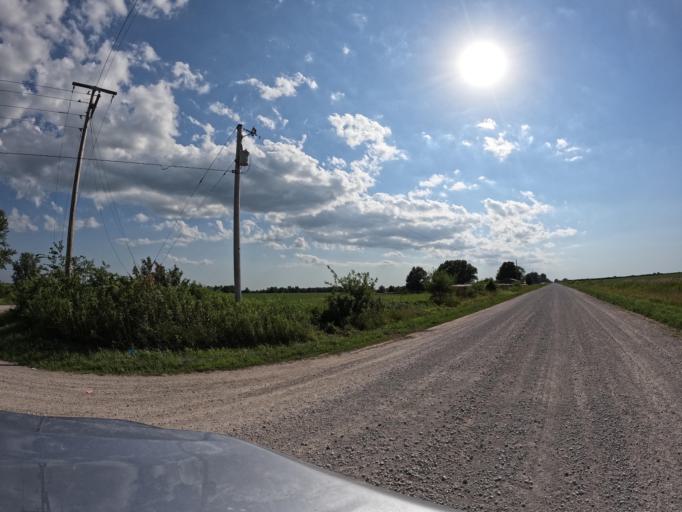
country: US
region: Iowa
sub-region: Appanoose County
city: Centerville
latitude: 40.7179
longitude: -93.0016
